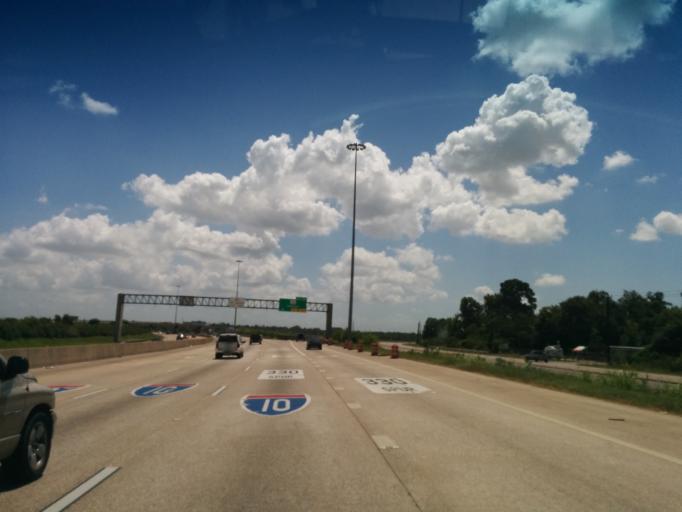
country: US
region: Texas
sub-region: Harris County
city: Highlands
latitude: 29.7903
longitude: -95.0542
